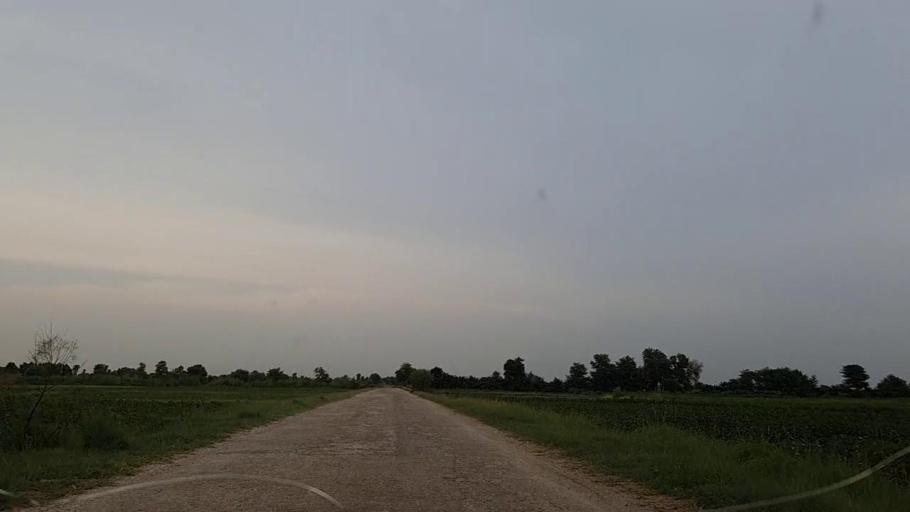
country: PK
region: Sindh
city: Mirpur Mathelo
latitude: 27.8760
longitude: 69.6365
